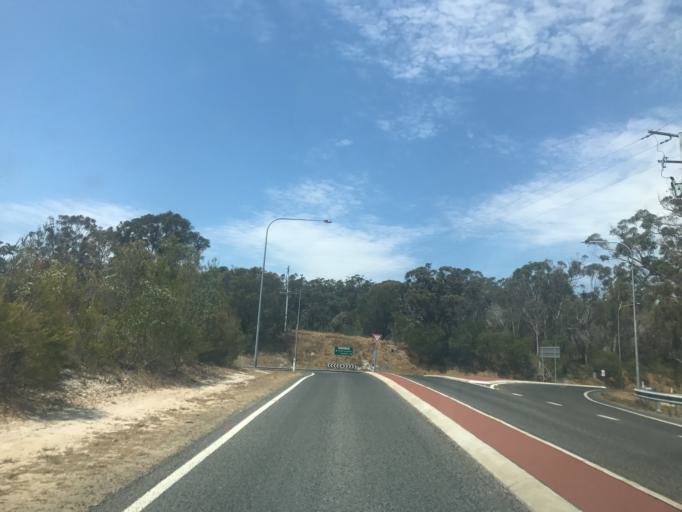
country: AU
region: Queensland
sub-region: Redland
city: Victoria Point
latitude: -27.4331
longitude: 153.4630
